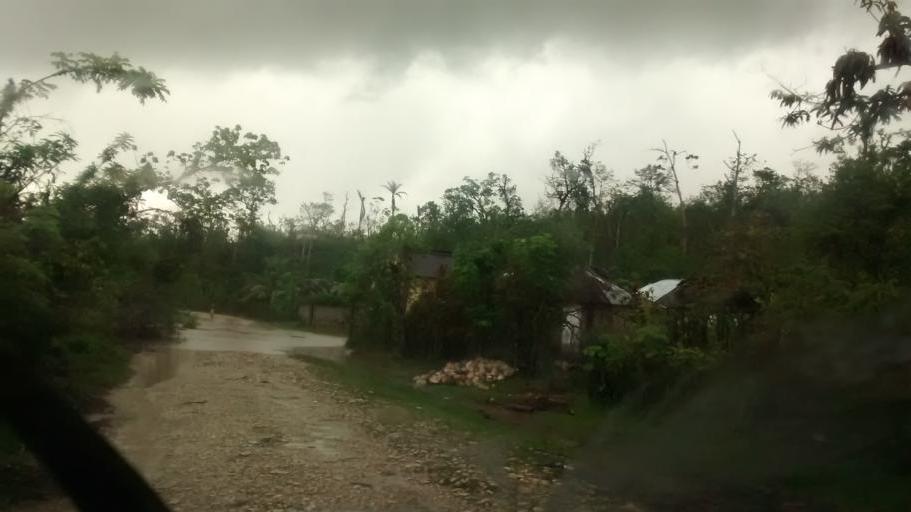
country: HT
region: Grandans
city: Corail
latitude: 18.5333
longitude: -73.9561
